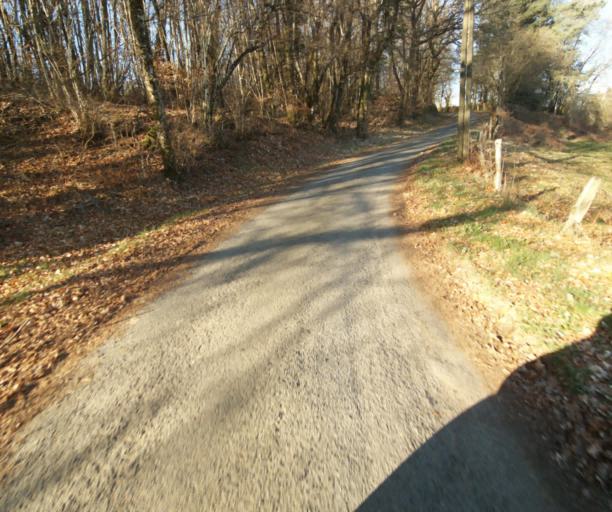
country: FR
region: Limousin
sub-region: Departement de la Correze
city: Uzerche
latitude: 45.3777
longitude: 1.5825
